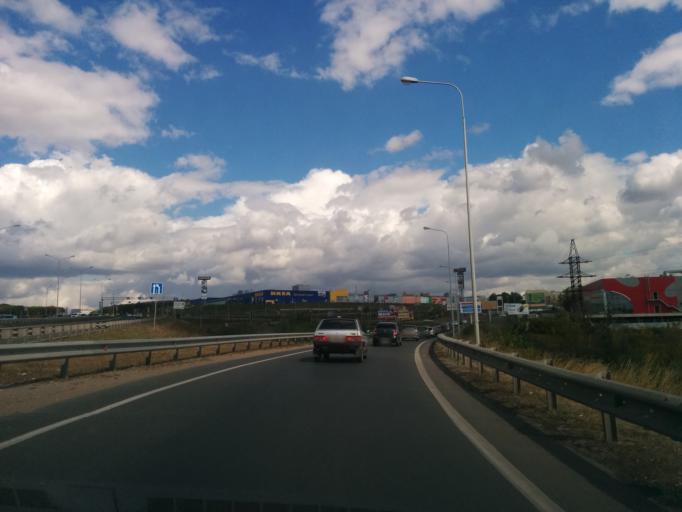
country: RU
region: Samara
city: Petra-Dubrava
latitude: 53.3193
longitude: 50.2971
